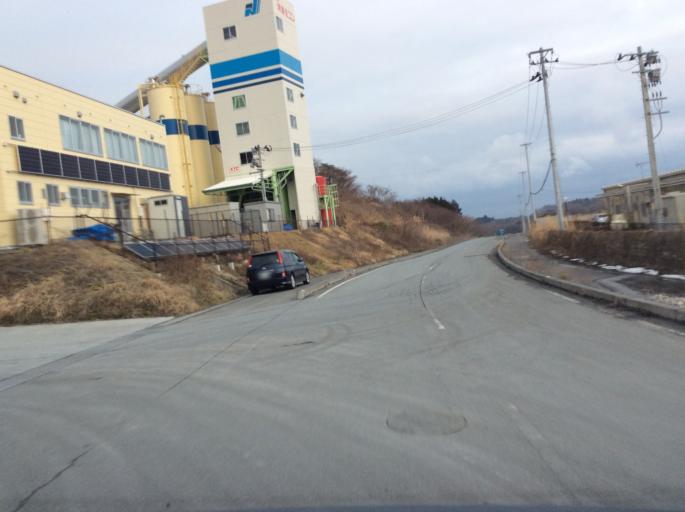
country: JP
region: Fukushima
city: Iwaki
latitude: 37.1280
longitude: 140.9726
